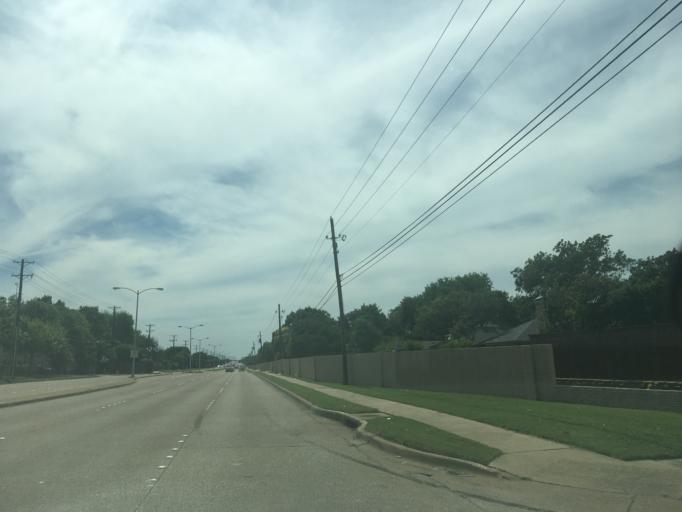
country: US
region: Texas
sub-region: Dallas County
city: Richardson
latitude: 32.9313
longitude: -96.6861
